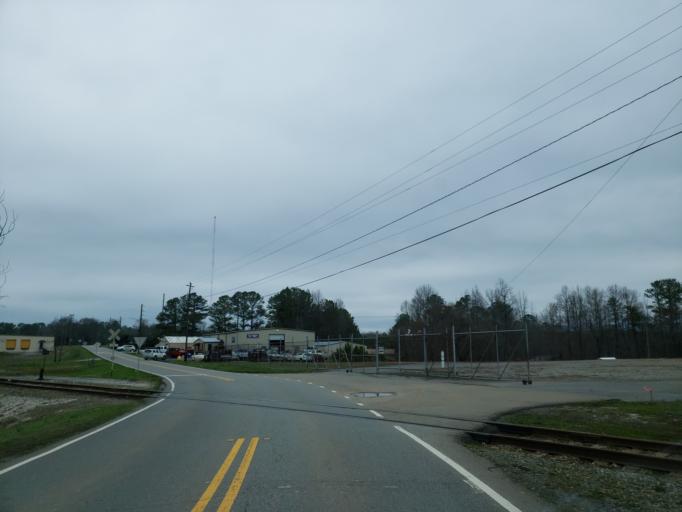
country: US
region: Georgia
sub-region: Pickens County
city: Jasper
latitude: 34.4747
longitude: -84.4372
